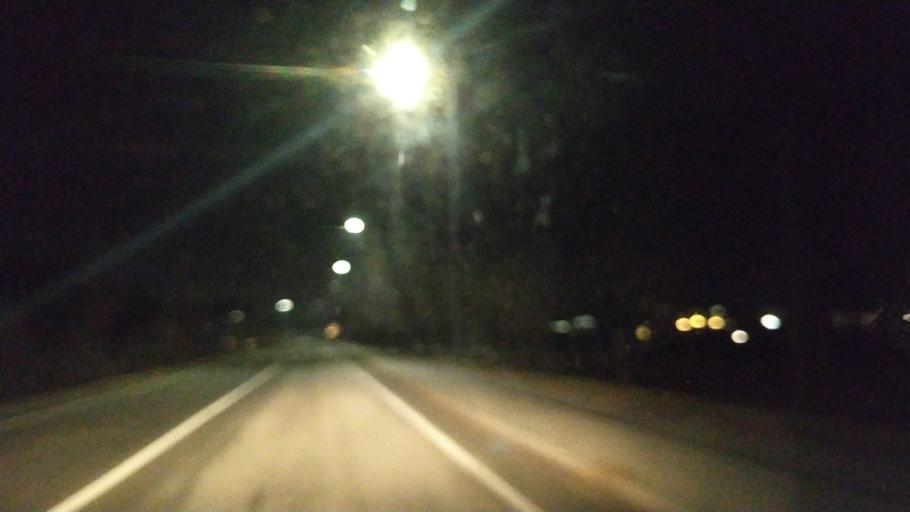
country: IT
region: Piedmont
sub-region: Provincia di Biella
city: Occhieppo Superiore
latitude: 45.5658
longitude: 8.0077
